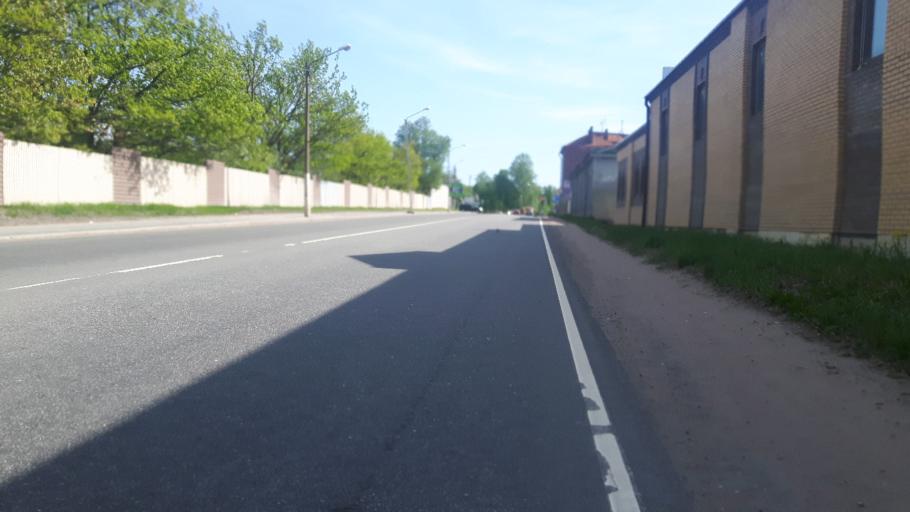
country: RU
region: Leningrad
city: Vyborg
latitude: 60.7219
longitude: 28.7170
